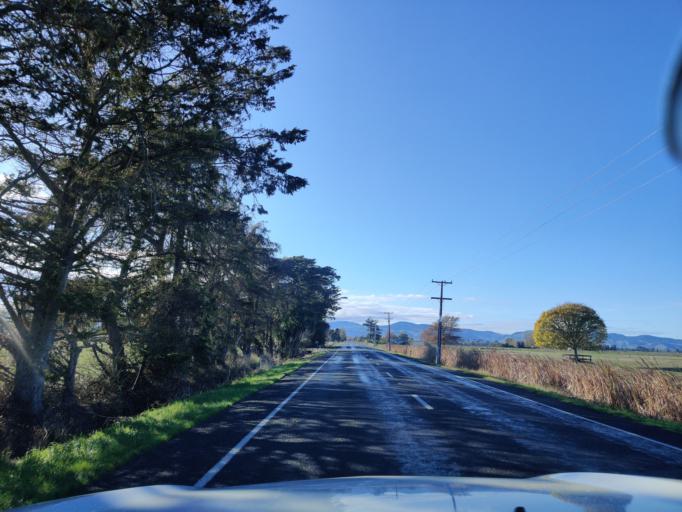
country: NZ
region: Waikato
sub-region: Hauraki District
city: Ngatea
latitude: -37.3110
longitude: 175.5706
